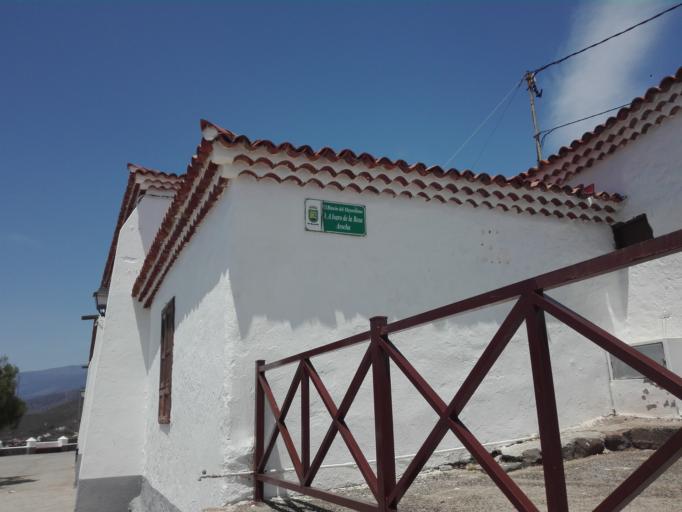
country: ES
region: Canary Islands
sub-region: Provincia de Santa Cruz de Tenerife
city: Candelaria
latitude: 28.4112
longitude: -16.3482
